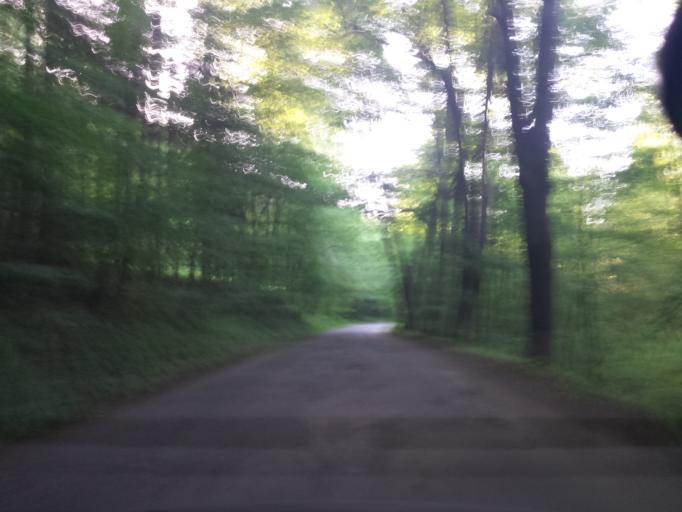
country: CZ
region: Central Bohemia
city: Mseno
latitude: 50.4852
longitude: 14.6033
